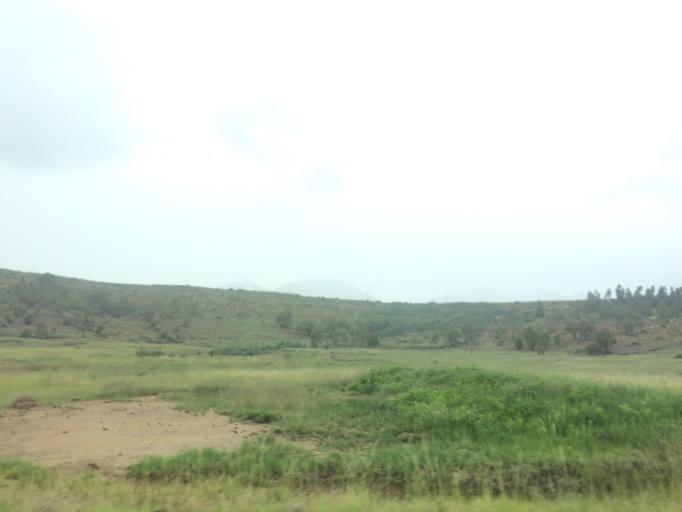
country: LS
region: Maseru
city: Nako
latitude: -29.7513
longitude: 27.5181
